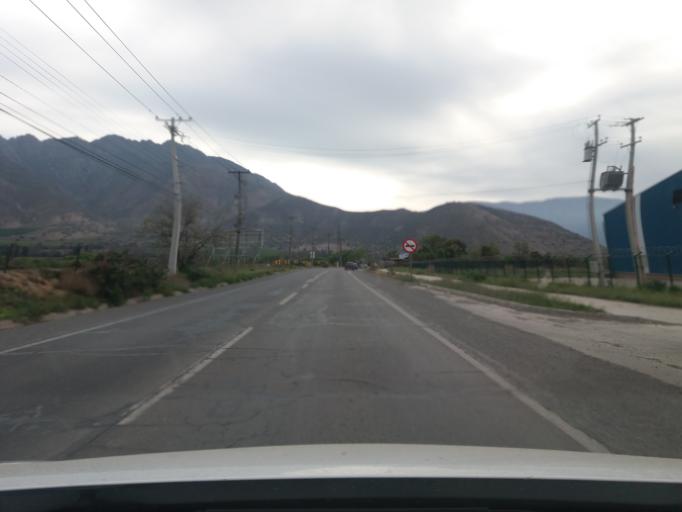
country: CL
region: Valparaiso
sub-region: Provincia de San Felipe
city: San Felipe
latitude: -32.7715
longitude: -70.7206
